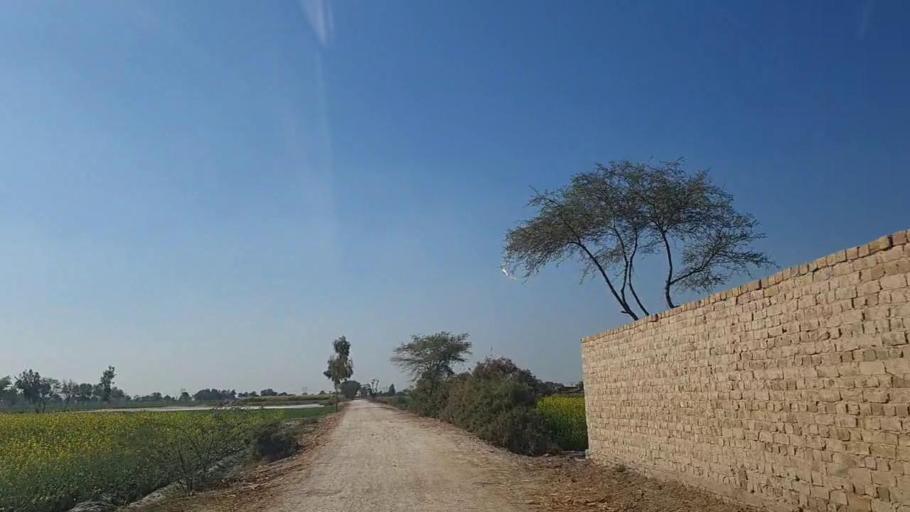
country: PK
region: Sindh
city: Sakrand
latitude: 26.2629
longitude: 68.2118
